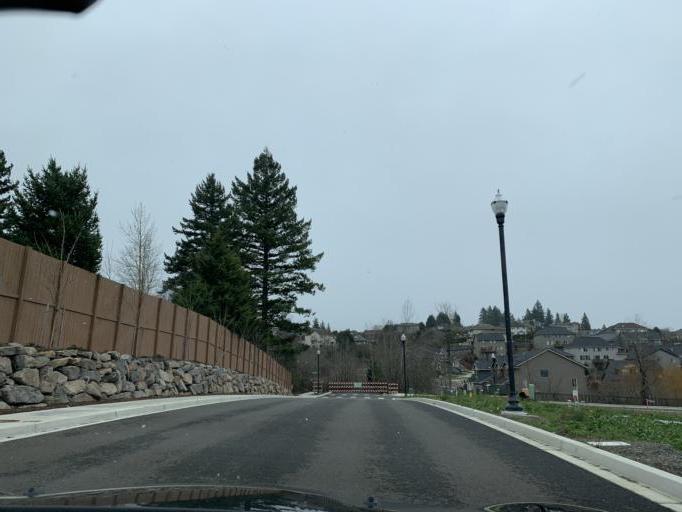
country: US
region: Washington
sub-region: Clark County
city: Mill Plain
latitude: 45.5905
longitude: -122.4675
